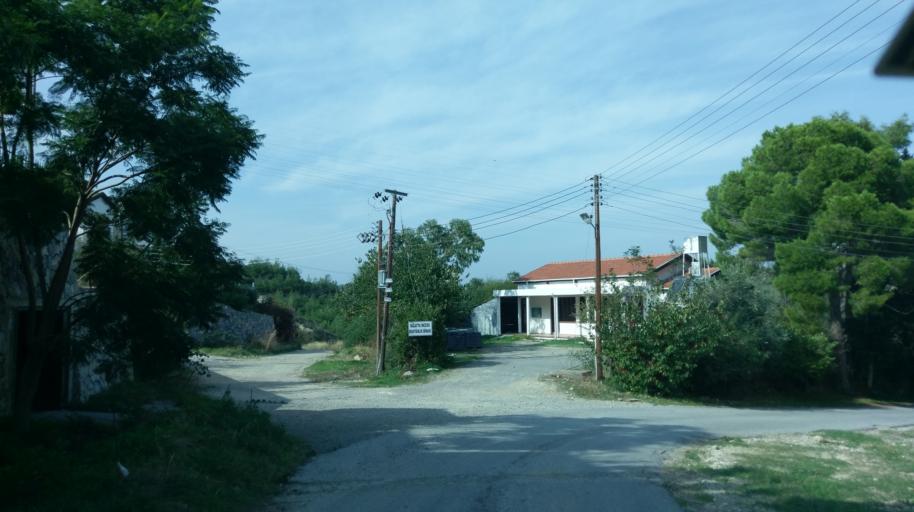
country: CY
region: Keryneia
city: Lapithos
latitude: 35.3278
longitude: 33.2057
